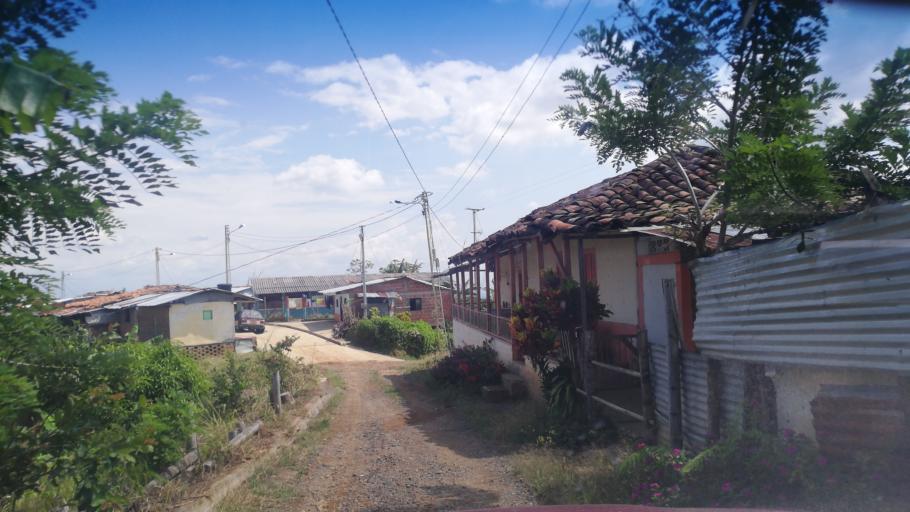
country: CO
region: Risaralda
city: Balboa
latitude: 4.9262
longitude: -75.9593
